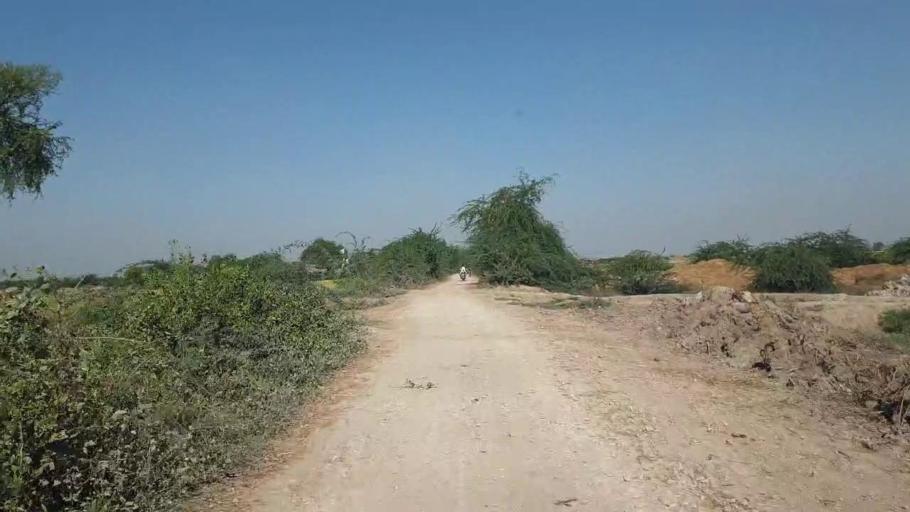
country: PK
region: Sindh
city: Talhar
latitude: 24.7794
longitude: 68.7856
